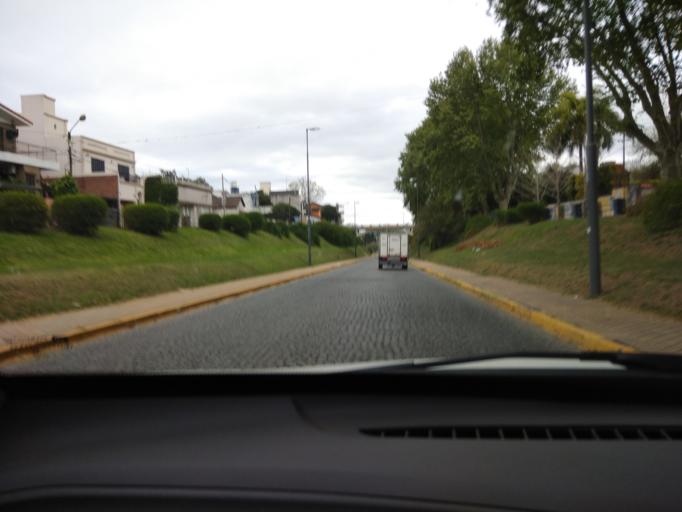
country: AR
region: Santa Fe
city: Granadero Baigorria
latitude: -32.8942
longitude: -60.6894
